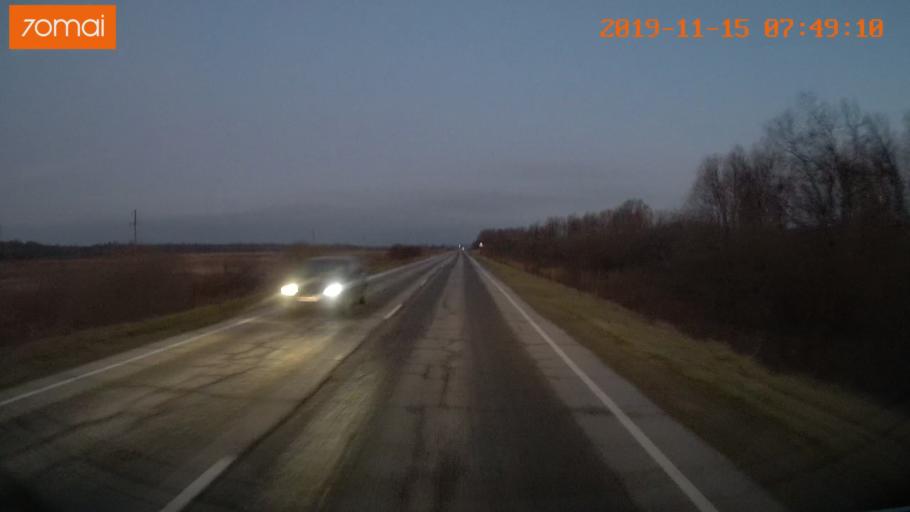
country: RU
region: Vologda
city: Cherepovets
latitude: 58.8582
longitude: 38.2339
